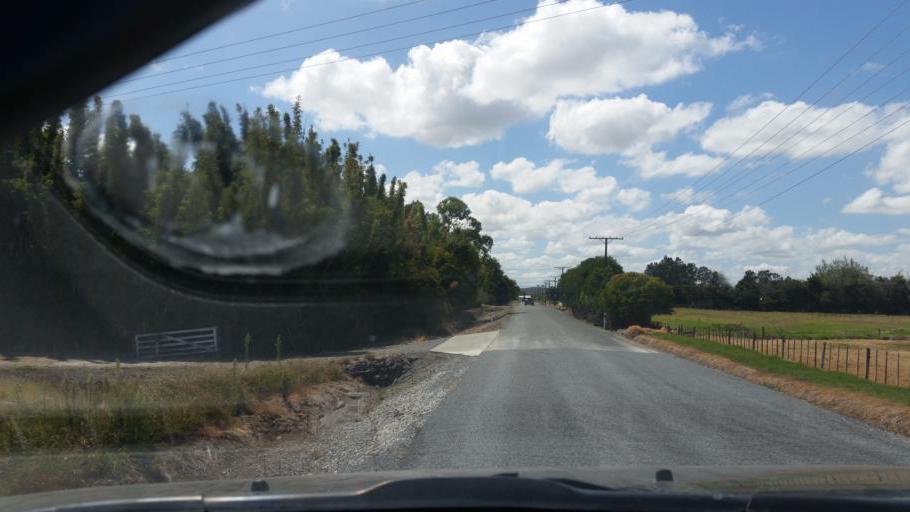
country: NZ
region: Northland
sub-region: Kaipara District
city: Dargaville
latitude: -35.9441
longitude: 173.8533
